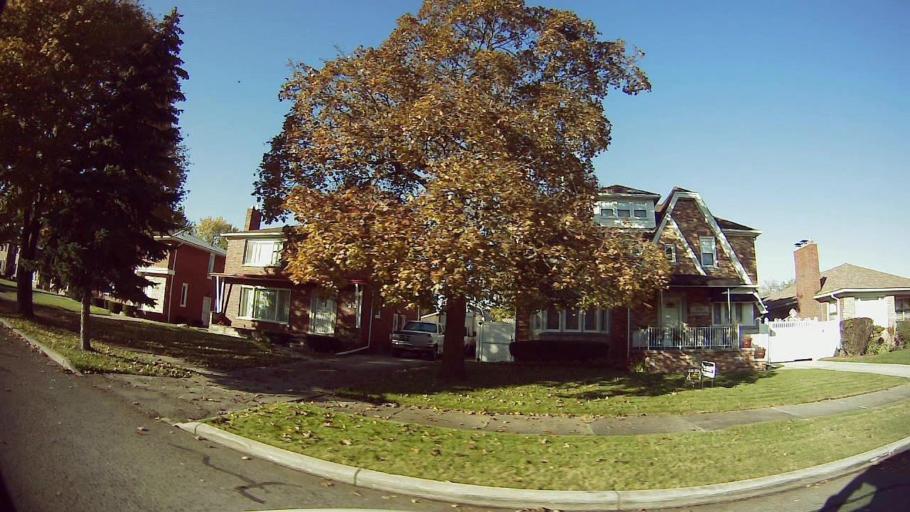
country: US
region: Michigan
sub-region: Wayne County
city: Dearborn
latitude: 42.3530
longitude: -83.1701
